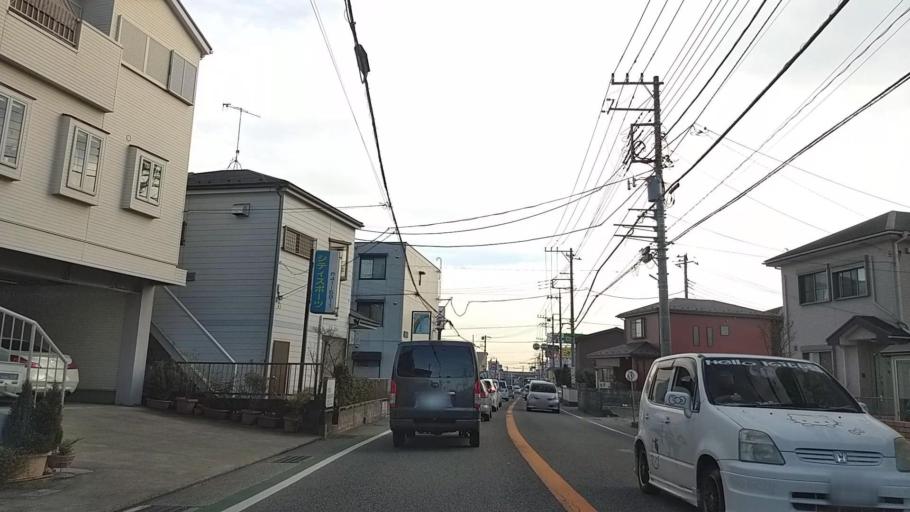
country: JP
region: Kanagawa
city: Atsugi
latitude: 35.4772
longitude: 139.3431
